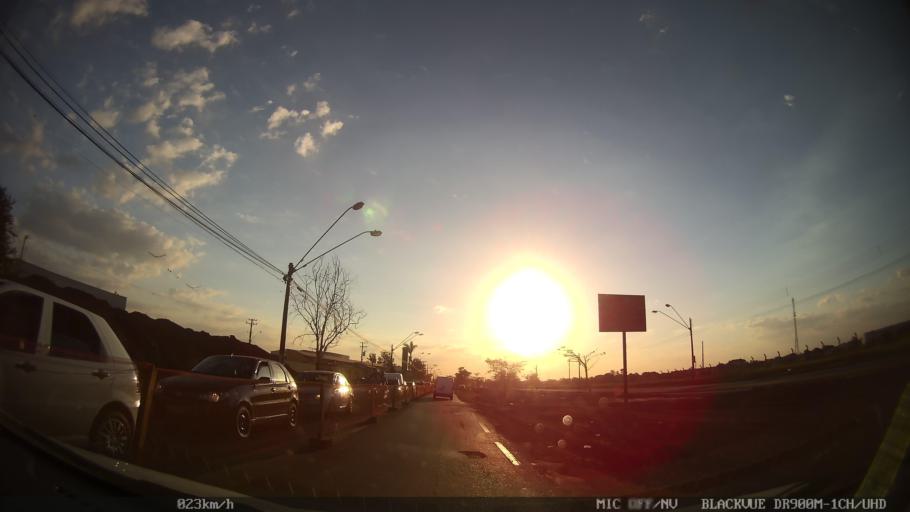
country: BR
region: Sao Paulo
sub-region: Ribeirao Preto
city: Ribeirao Preto
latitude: -21.1427
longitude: -47.7796
